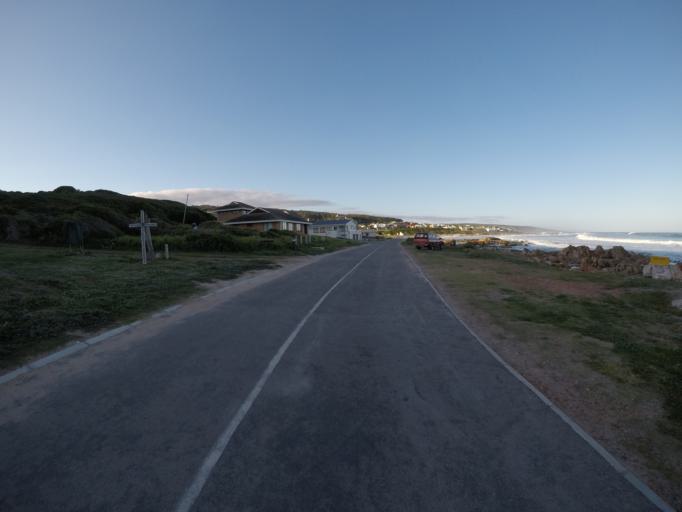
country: ZA
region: Western Cape
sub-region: Eden District Municipality
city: Riversdale
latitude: -34.4287
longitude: 21.3360
